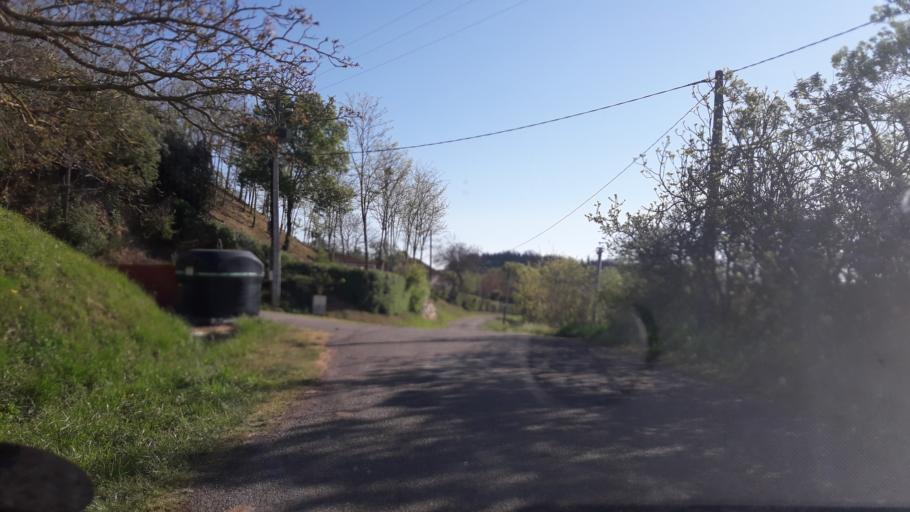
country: FR
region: Midi-Pyrenees
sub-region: Departement de la Haute-Garonne
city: Montesquieu-Volvestre
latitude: 43.2002
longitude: 1.2810
